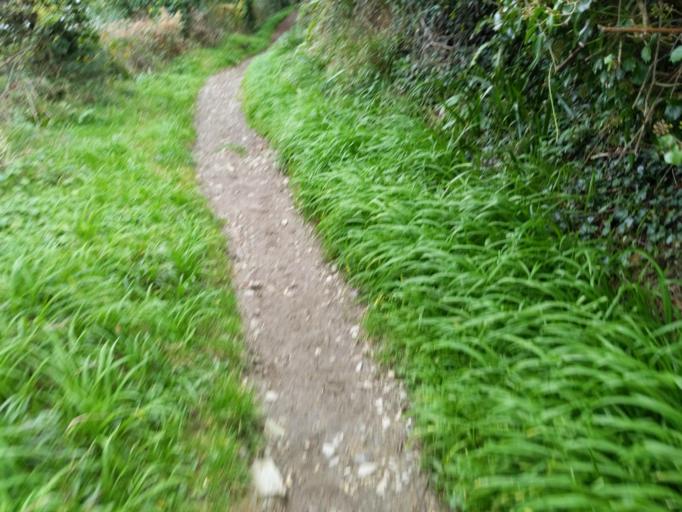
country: GB
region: England
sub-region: Cornwall
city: Looe
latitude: 50.3633
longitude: -4.4295
